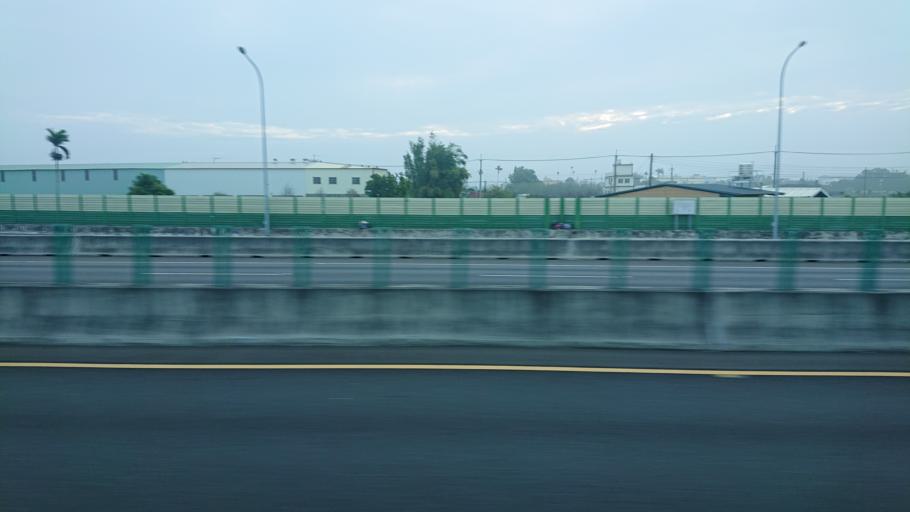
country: TW
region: Taiwan
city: Fengyuan
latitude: 24.2954
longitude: 120.6959
